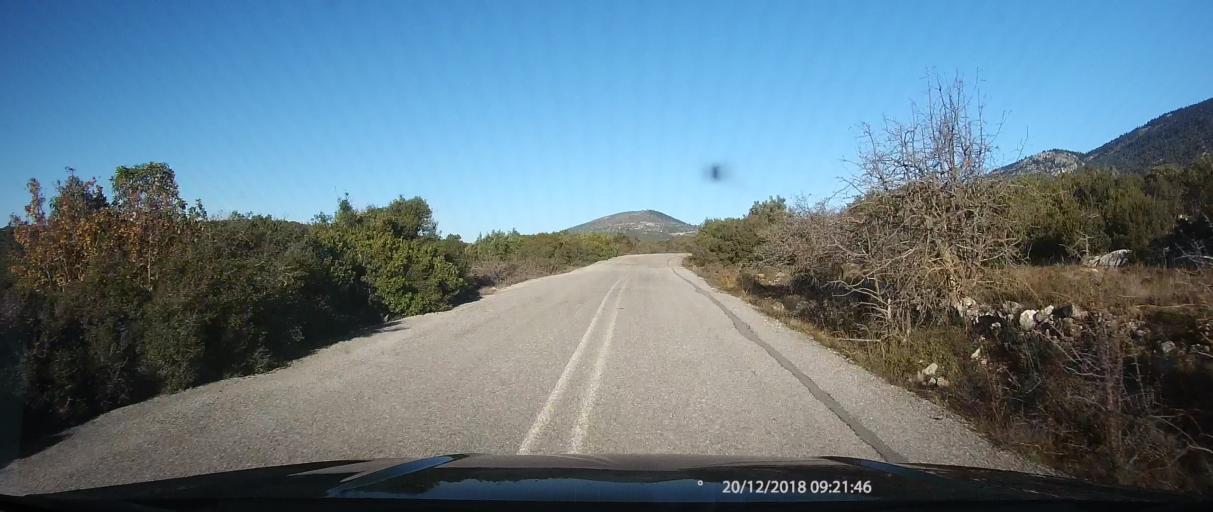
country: GR
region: Peloponnese
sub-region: Nomos Lakonias
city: Molaoi
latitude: 36.9427
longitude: 22.9132
